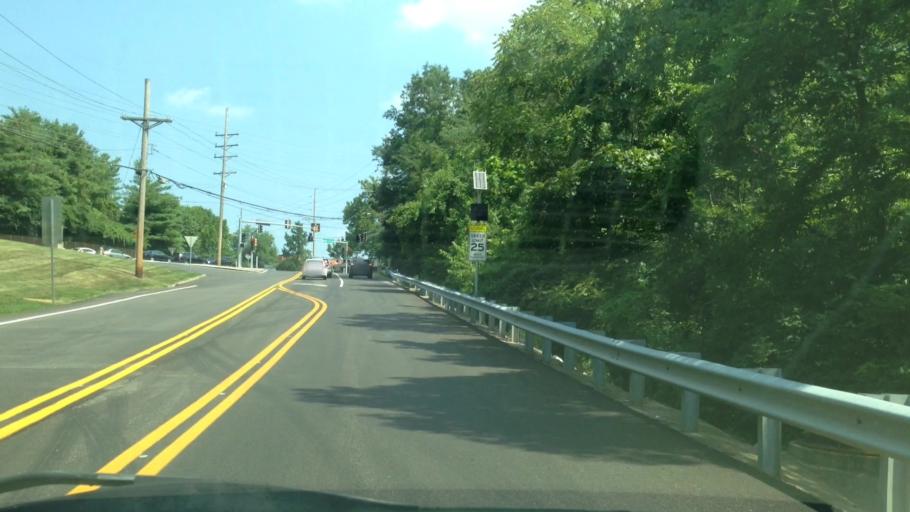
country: US
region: Missouri
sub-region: Saint Louis County
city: Des Peres
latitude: 38.5831
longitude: -90.4437
